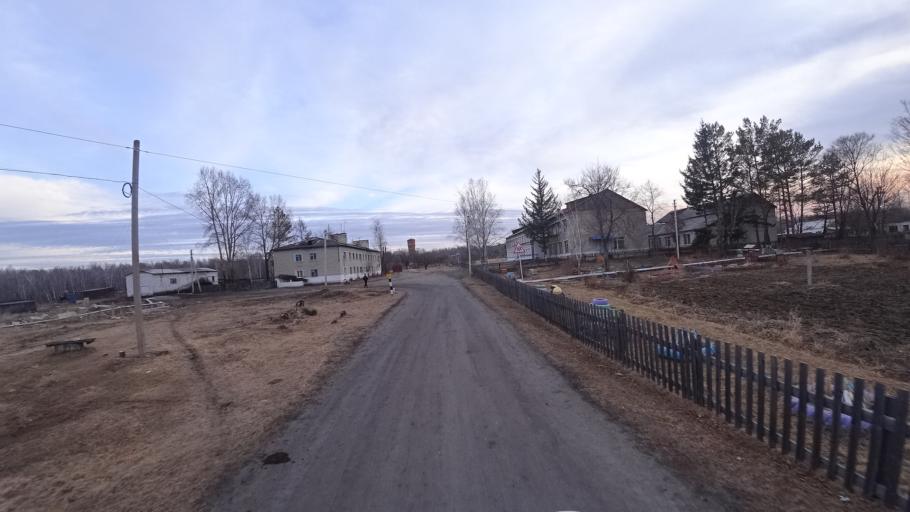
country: RU
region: Amur
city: Bureya
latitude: 50.0188
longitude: 129.7703
